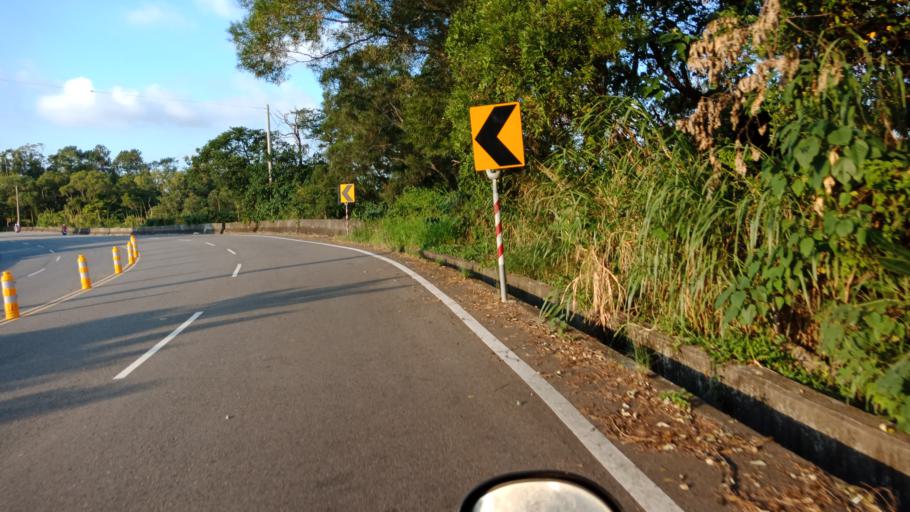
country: TW
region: Taiwan
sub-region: Hsinchu
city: Hsinchu
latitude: 24.7587
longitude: 120.9992
